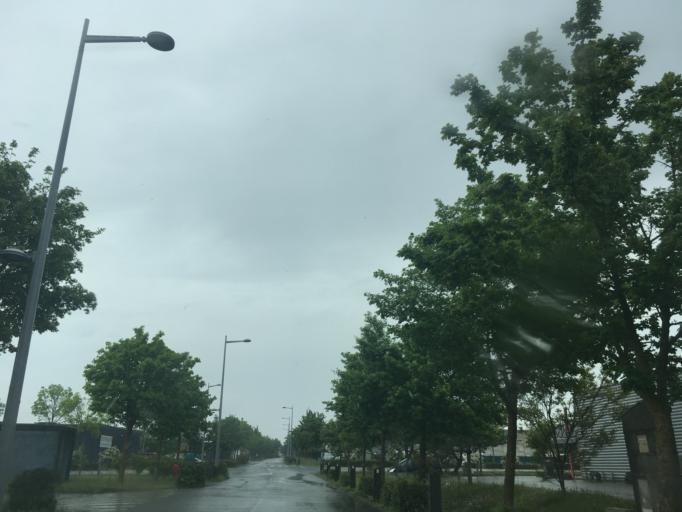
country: FR
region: Poitou-Charentes
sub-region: Departement de la Charente
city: Saint-Brice
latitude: 45.6751
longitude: -0.3069
